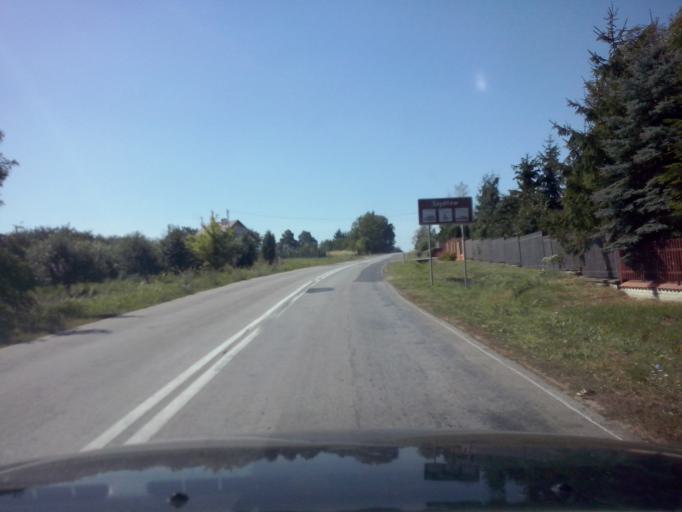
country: PL
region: Swietokrzyskie
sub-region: Powiat staszowski
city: Szydlow
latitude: 50.5938
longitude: 21.0099
